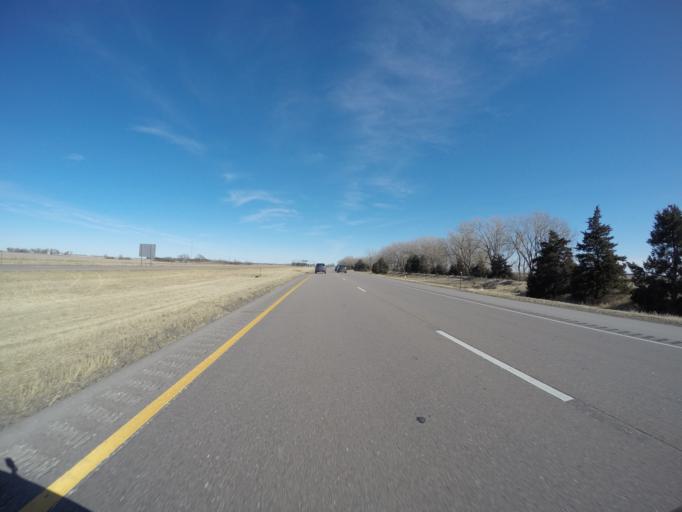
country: US
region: Nebraska
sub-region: York County
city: York
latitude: 40.8220
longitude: -97.5726
